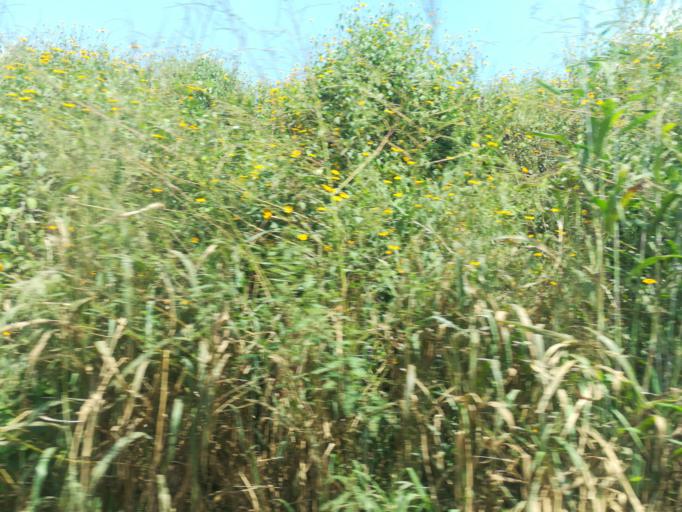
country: NG
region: Ogun
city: Abeokuta
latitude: 7.1400
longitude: 3.4012
